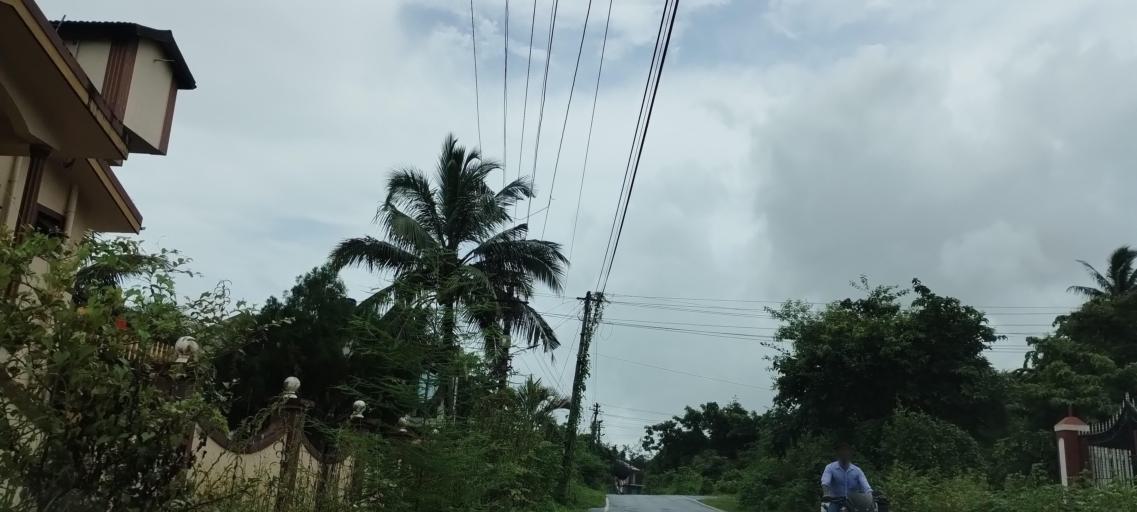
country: IN
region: Goa
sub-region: North Goa
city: Aldona
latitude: 15.5824
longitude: 73.8669
